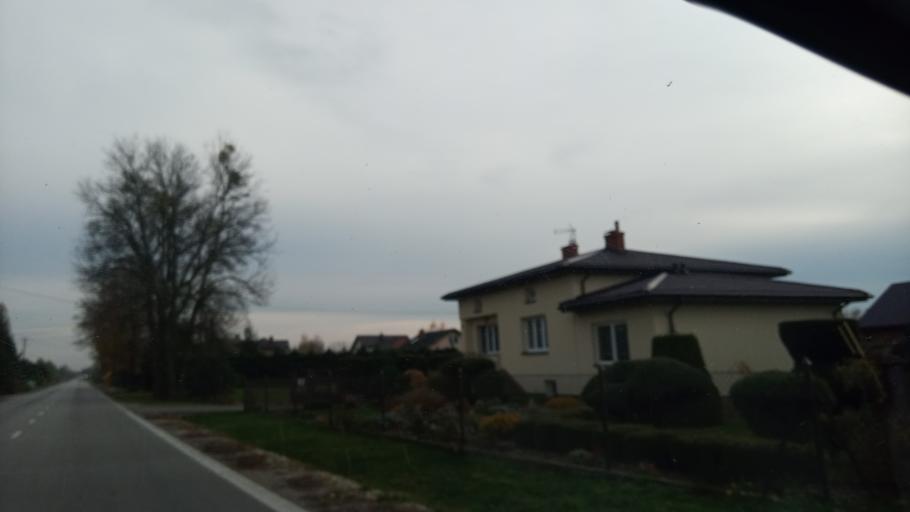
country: PL
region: Lodz Voivodeship
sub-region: Powiat skierniewicki
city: Bolimow
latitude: 52.1611
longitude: 20.1802
